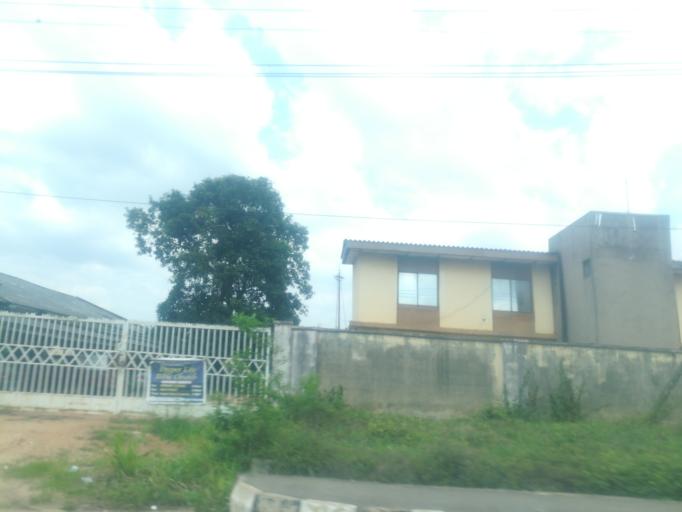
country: NG
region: Oyo
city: Ibadan
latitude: 7.4079
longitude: 3.8684
